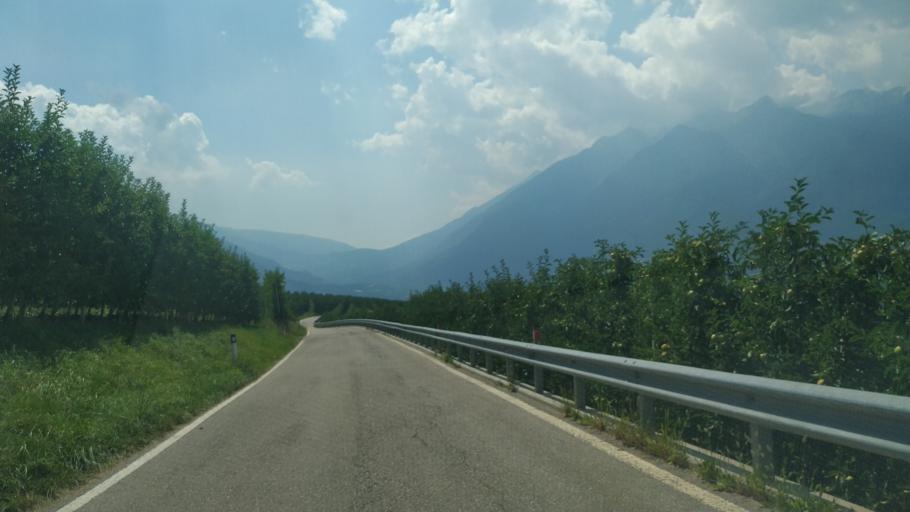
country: IT
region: Trentino-Alto Adige
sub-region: Provincia di Trento
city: Vigo di Ton
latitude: 46.2709
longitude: 11.0823
